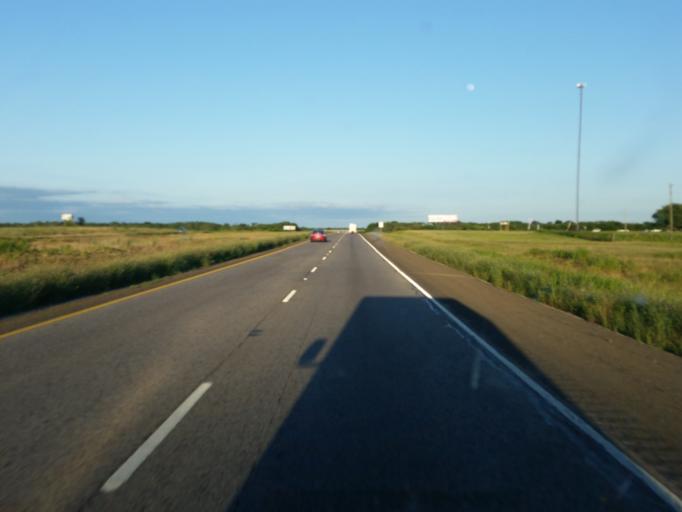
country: US
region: Texas
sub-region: Van Zandt County
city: Wills Point
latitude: 32.6530
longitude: -96.0855
